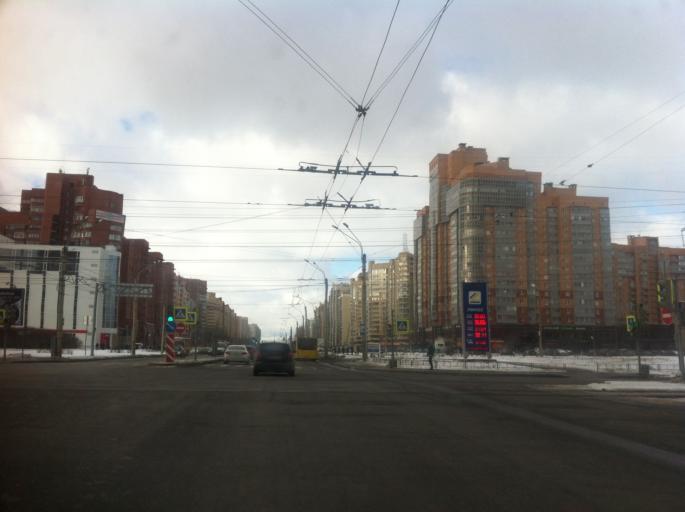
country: RU
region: St.-Petersburg
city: Uritsk
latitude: 59.8561
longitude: 30.2030
